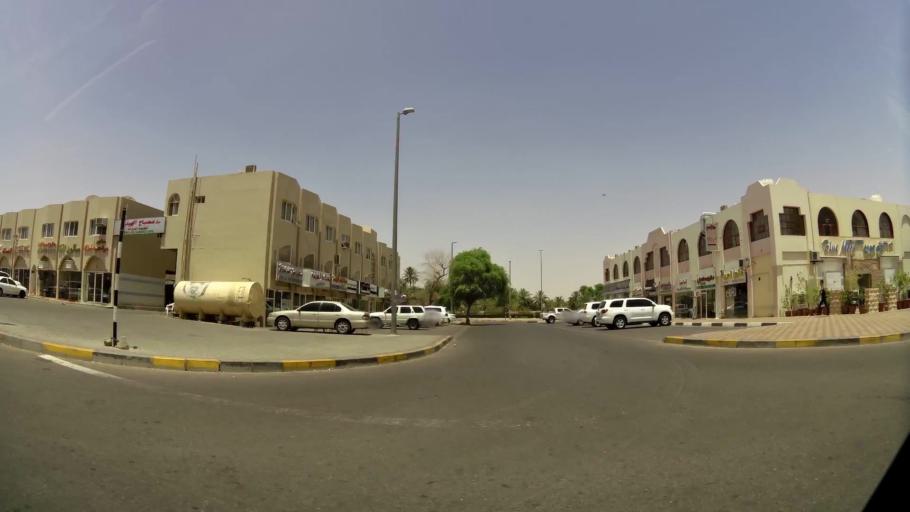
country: OM
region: Al Buraimi
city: Al Buraymi
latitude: 24.2661
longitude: 55.7680
